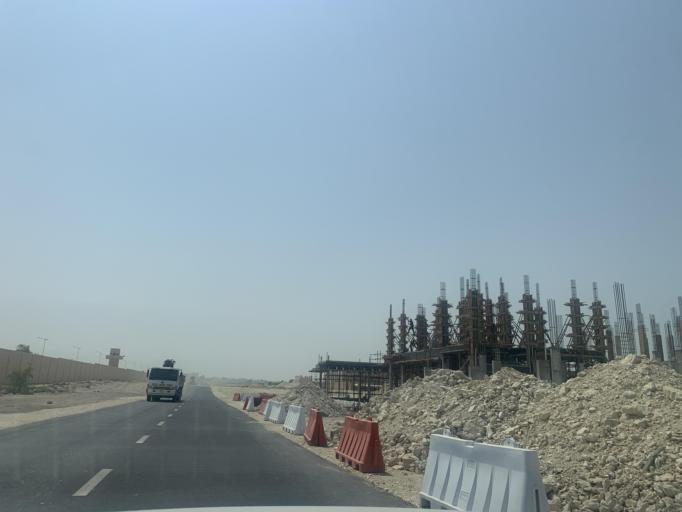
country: BH
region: Central Governorate
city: Madinat Hamad
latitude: 26.1487
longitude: 50.4768
